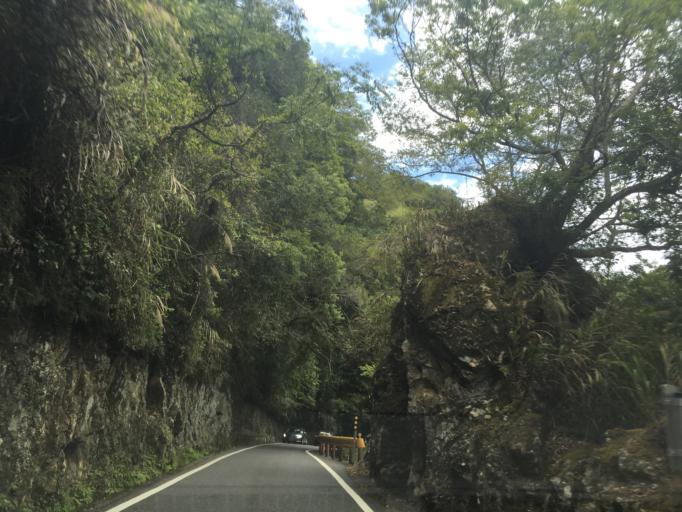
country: TW
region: Taiwan
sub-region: Hualien
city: Hualian
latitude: 24.1964
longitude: 121.4735
